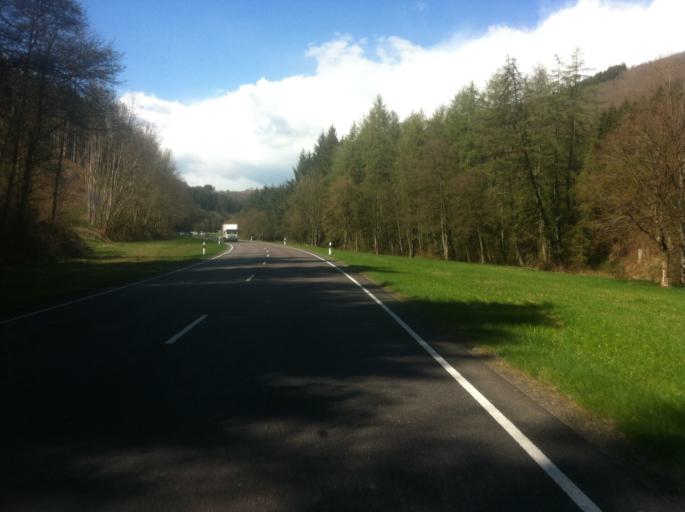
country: LU
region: Diekirch
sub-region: Canton de Wiltz
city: Esch-sur-Sure
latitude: 49.9254
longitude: 5.9423
